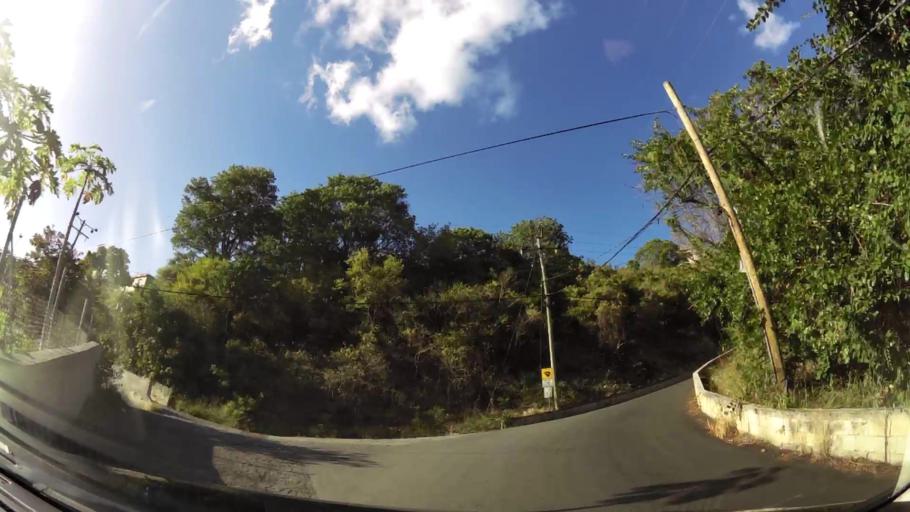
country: VG
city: Road Town
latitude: 18.4310
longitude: -64.6599
